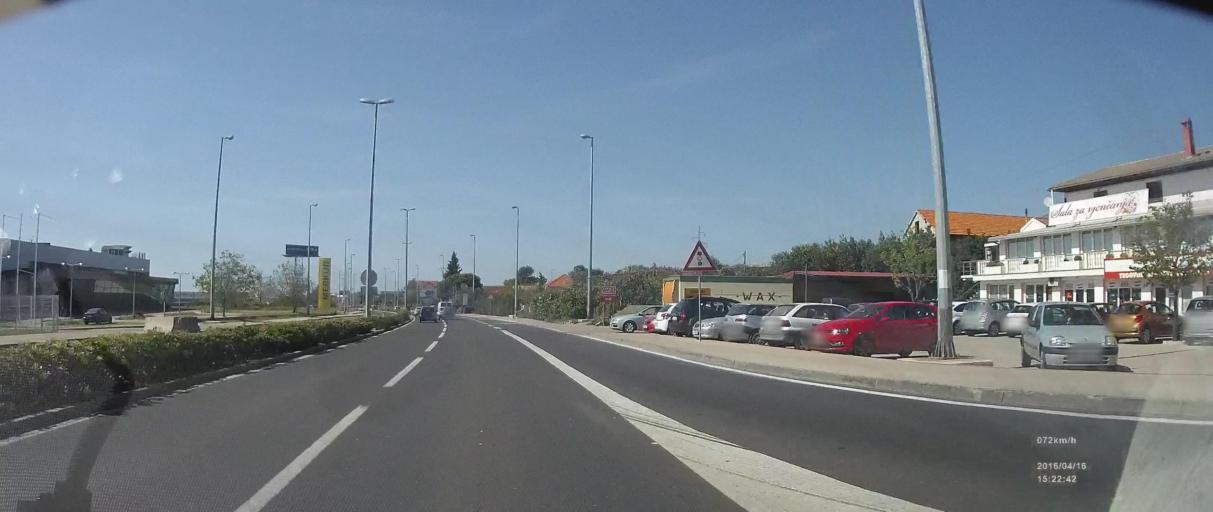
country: HR
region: Zadarska
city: Zadar
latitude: 44.0976
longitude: 15.2716
